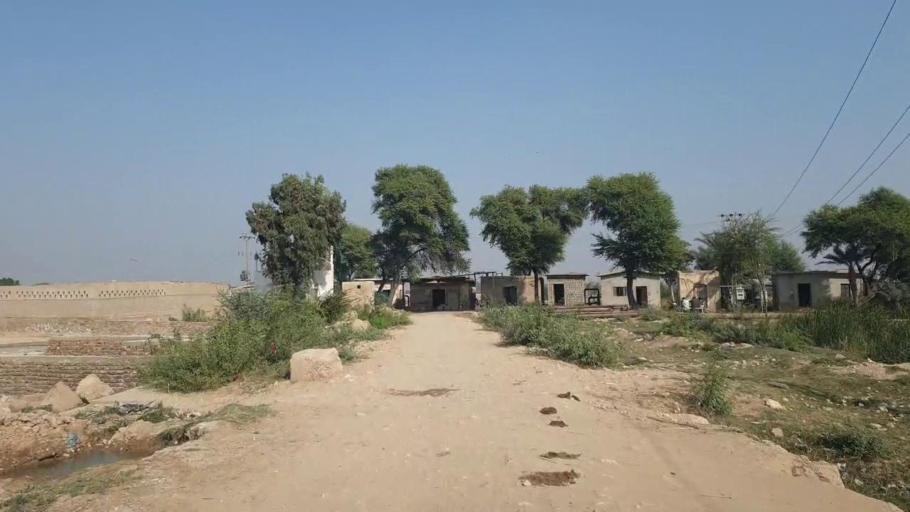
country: PK
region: Sindh
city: Kotri
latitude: 25.3644
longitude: 68.2885
